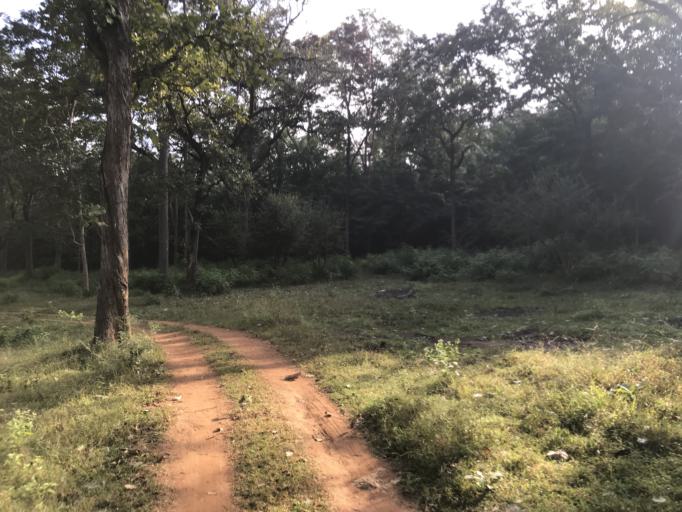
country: IN
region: Karnataka
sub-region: Mysore
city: Heggadadevankote
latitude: 11.9416
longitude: 76.2008
